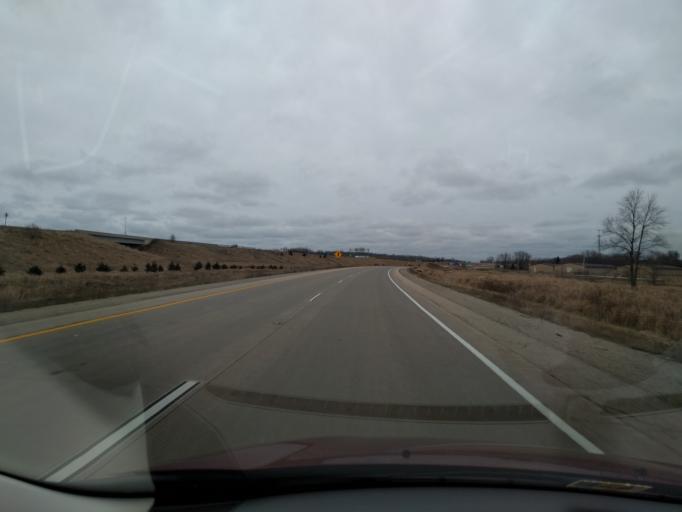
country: US
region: Wisconsin
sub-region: Winnebago County
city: Winneconne
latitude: 44.2074
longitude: -88.6852
